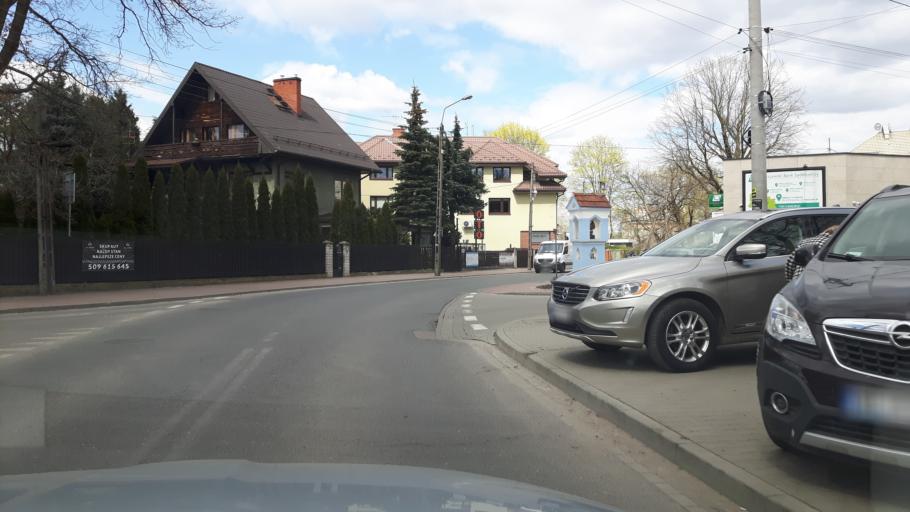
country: PL
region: Masovian Voivodeship
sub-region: Powiat wolominski
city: Kobylka
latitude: 52.3342
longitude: 21.2152
